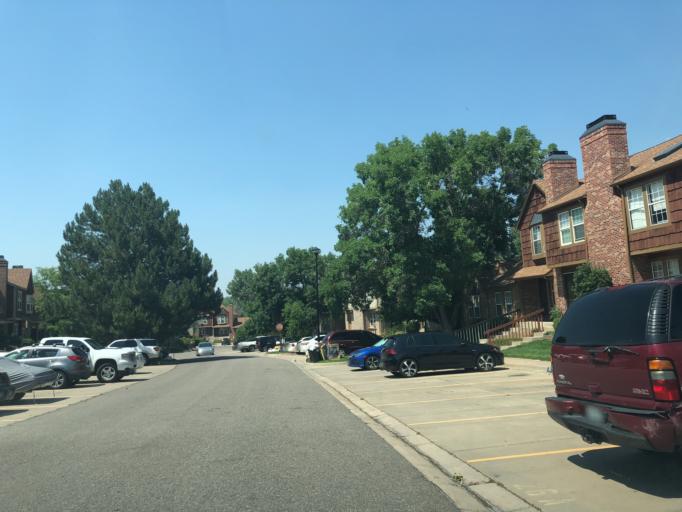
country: US
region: Colorado
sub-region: Arapahoe County
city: Dove Valley
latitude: 39.6345
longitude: -104.7861
